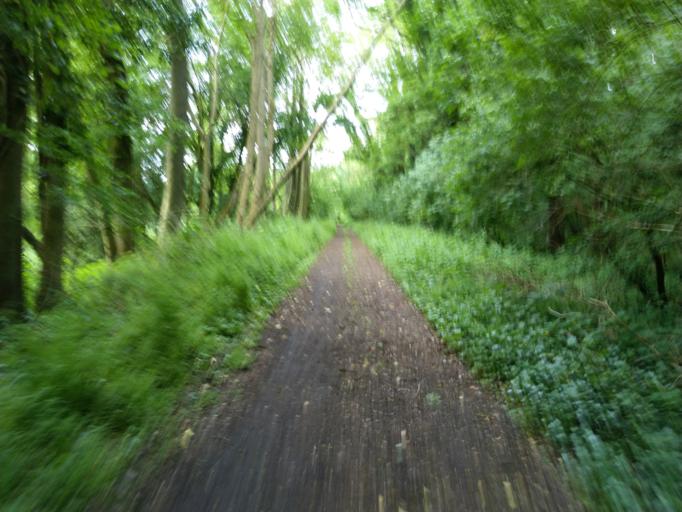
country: FR
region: Picardie
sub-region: Departement de l'Aisne
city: Guise
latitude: 49.9271
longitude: 3.5986
